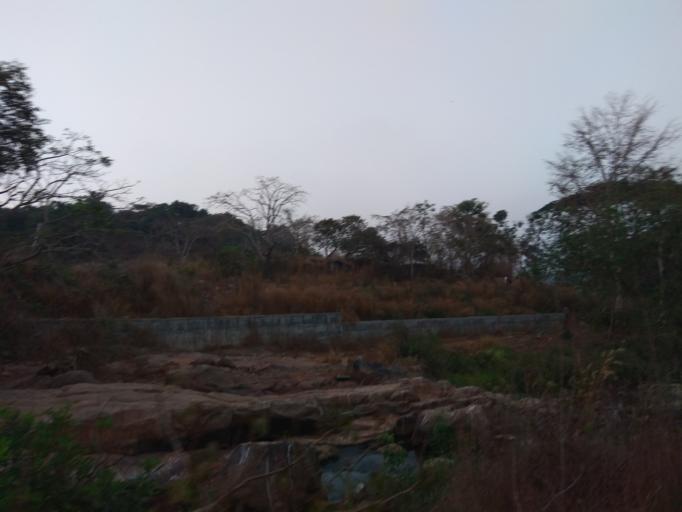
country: IN
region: Karnataka
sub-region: Dakshina Kannada
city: Mangalore
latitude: 12.9282
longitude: 74.8774
